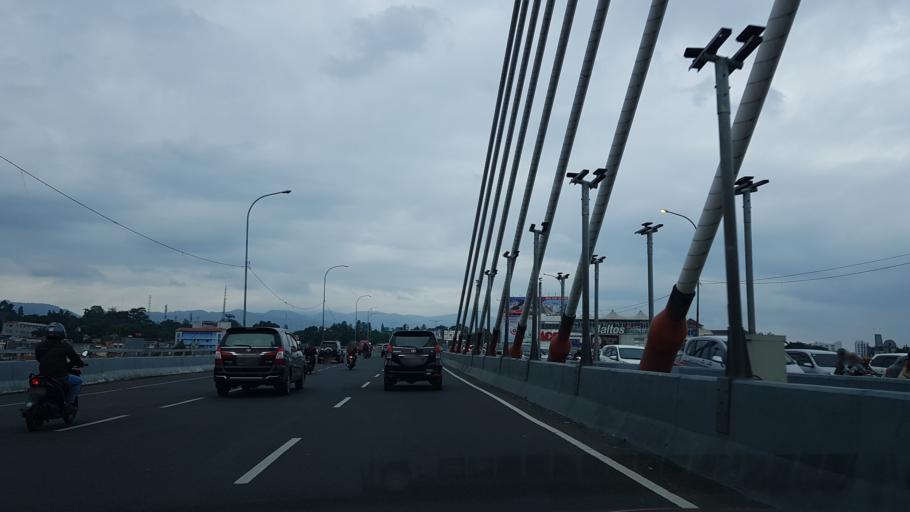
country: ID
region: West Java
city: Bandung
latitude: -6.8994
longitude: 107.6059
